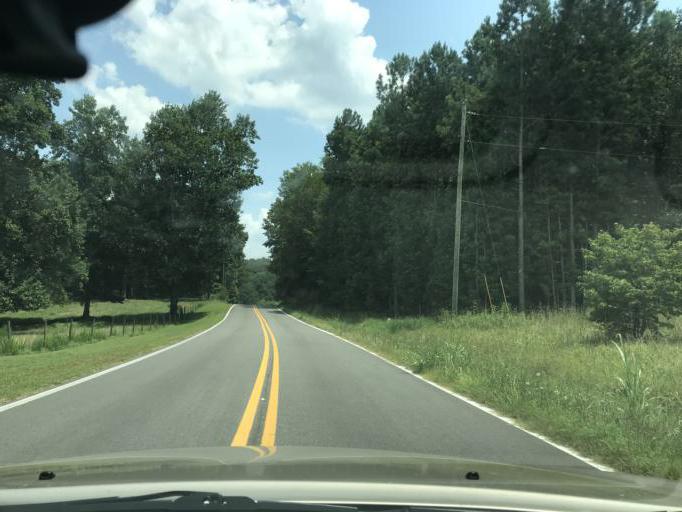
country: US
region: Georgia
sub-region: Forsyth County
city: Cumming
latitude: 34.2668
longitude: -84.2314
